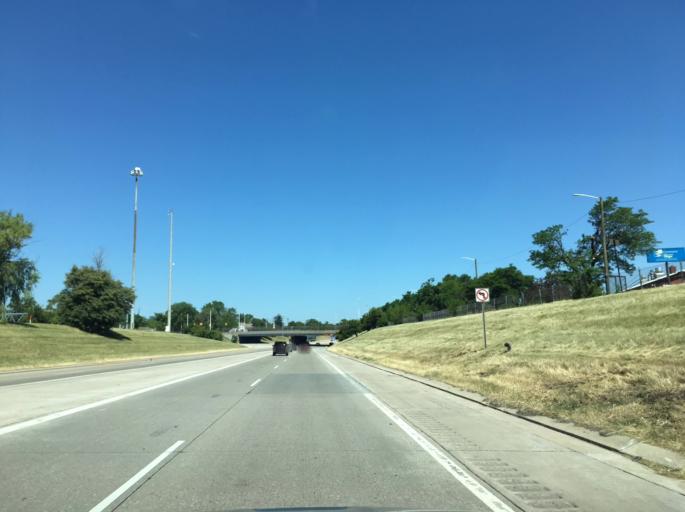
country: US
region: Michigan
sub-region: Wayne County
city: Detroit
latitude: 42.3344
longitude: -83.0881
